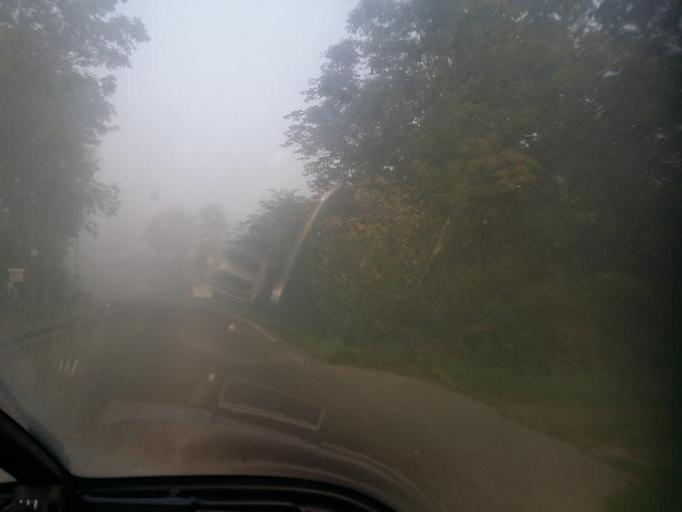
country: DE
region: Schleswig-Holstein
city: Elisabeth-Sophien-Koog
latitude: 54.4921
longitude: 8.8662
